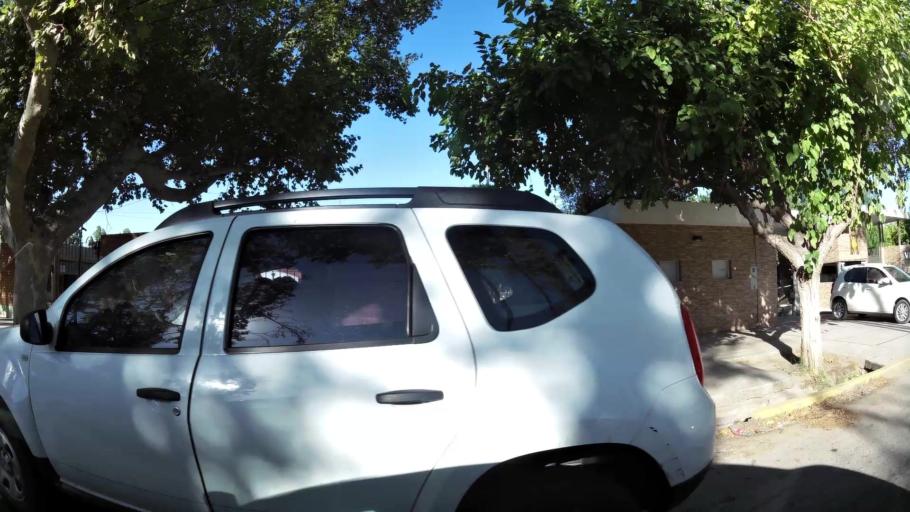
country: AR
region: San Juan
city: Villa Krause
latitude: -31.5694
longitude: -68.5197
